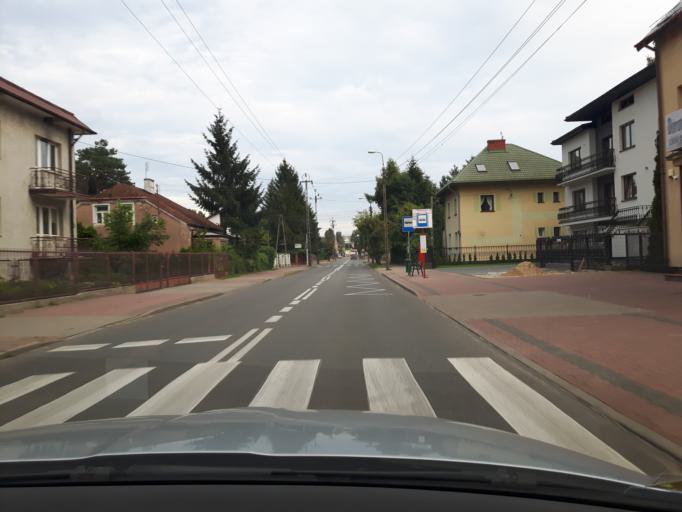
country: PL
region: Masovian Voivodeship
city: Zielonka
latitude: 52.3062
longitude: 21.1574
